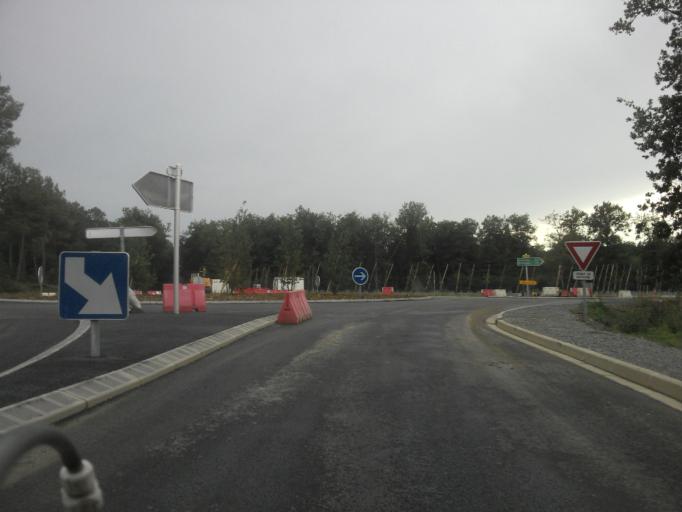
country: FR
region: Pays de la Loire
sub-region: Departement de Maine-et-Loire
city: Breze
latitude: 47.0936
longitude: -0.0011
